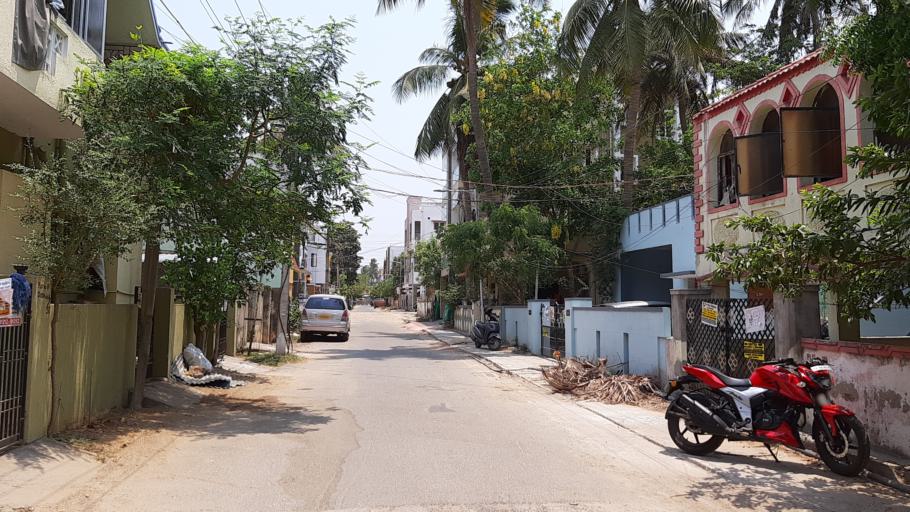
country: IN
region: Tamil Nadu
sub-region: Kancheepuram
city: Manappakkam
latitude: 13.0282
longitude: 80.1860
